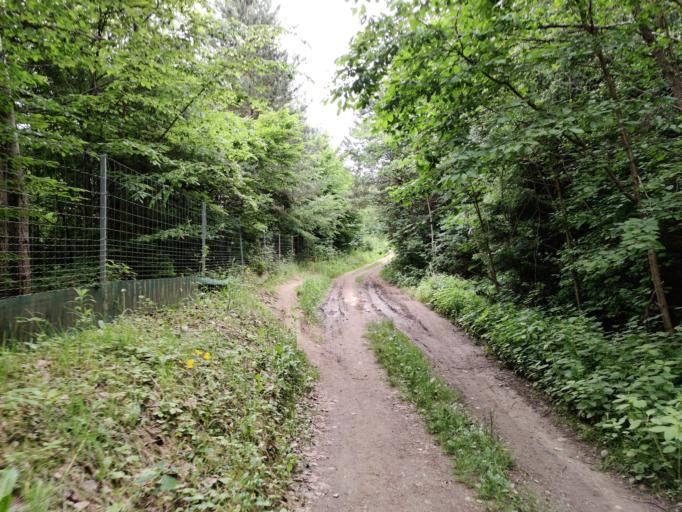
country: AT
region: Carinthia
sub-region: Klagenfurt am Woerthersee
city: Klagenfurt am Woerthersee
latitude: 46.6336
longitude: 14.2444
